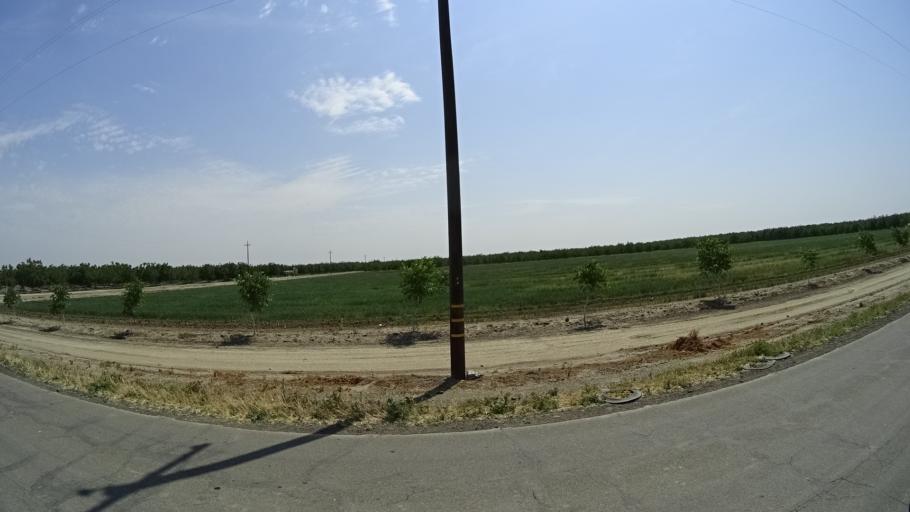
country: US
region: California
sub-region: Kings County
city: Armona
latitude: 36.3505
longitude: -119.7449
